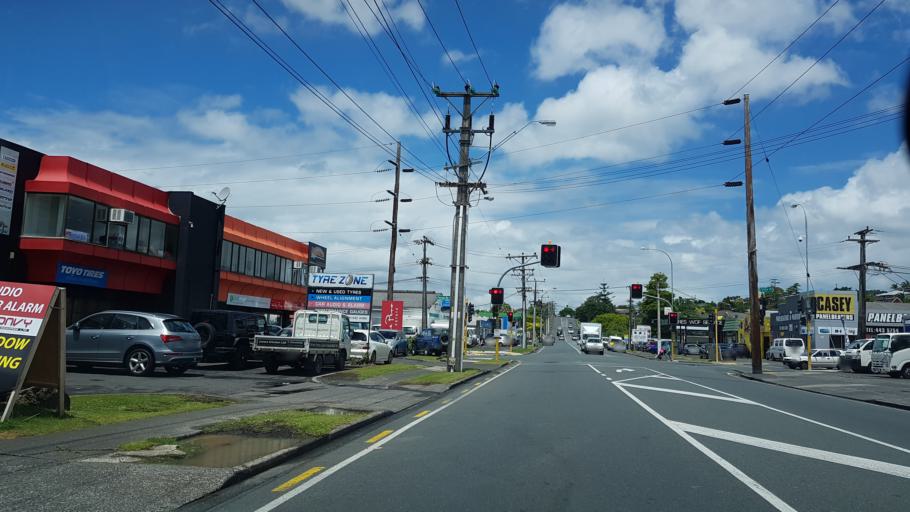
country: NZ
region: Auckland
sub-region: Auckland
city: North Shore
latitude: -36.7840
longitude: 174.7386
